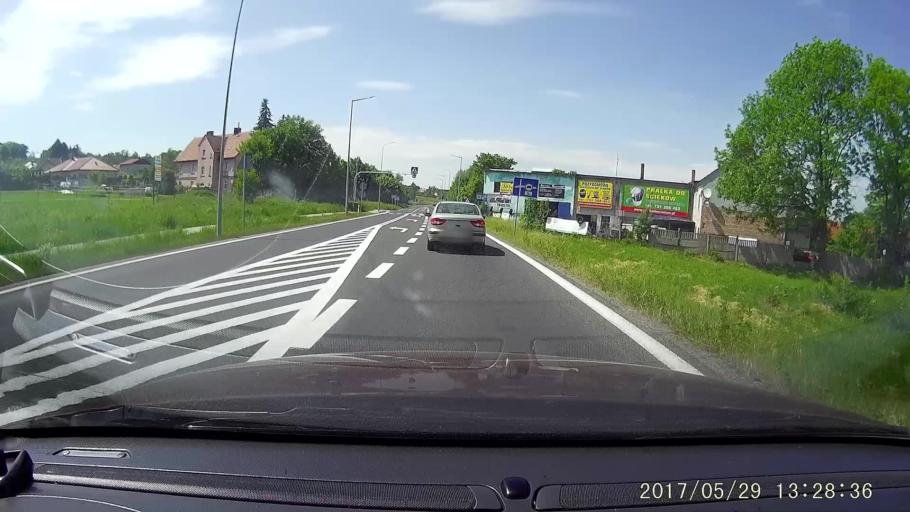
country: PL
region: Lower Silesian Voivodeship
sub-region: Powiat lubanski
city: Olszyna
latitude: 51.0651
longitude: 15.3713
